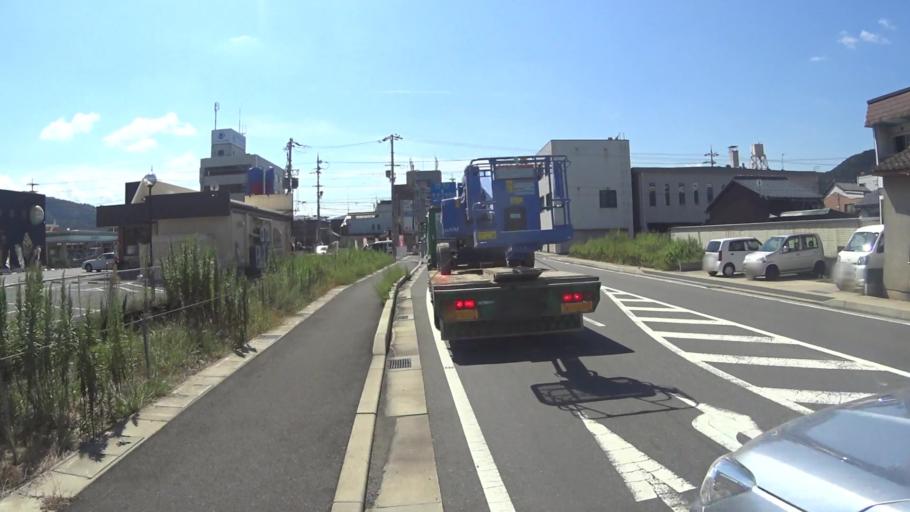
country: JP
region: Kyoto
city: Maizuru
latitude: 35.4516
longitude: 135.3292
